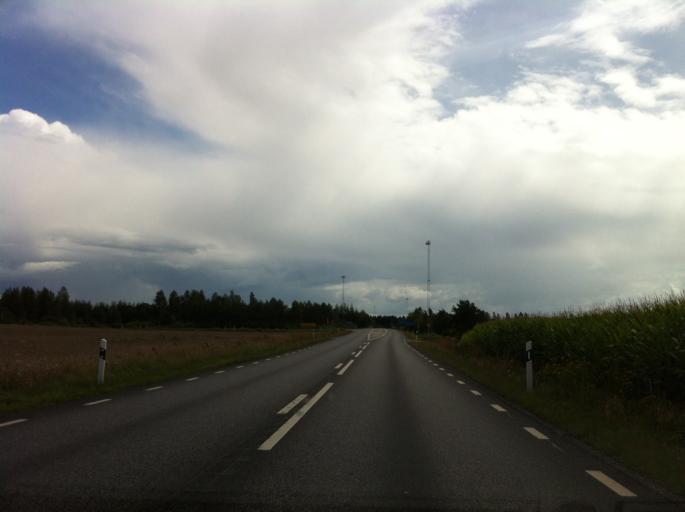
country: SE
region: Skane
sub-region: Hassleholms Kommun
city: Bjarnum
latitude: 56.2028
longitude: 13.6573
